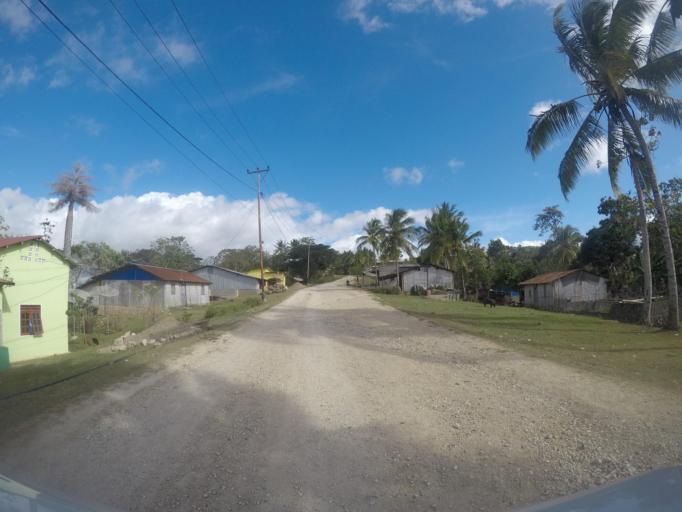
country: TL
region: Lautem
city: Lospalos
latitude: -8.5701
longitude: 126.8840
